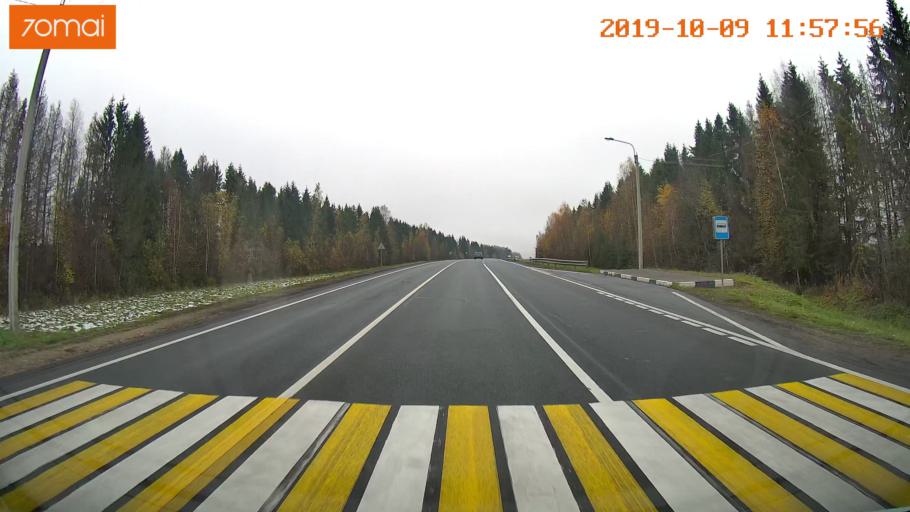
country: RU
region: Vologda
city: Gryazovets
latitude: 58.7251
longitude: 40.2954
